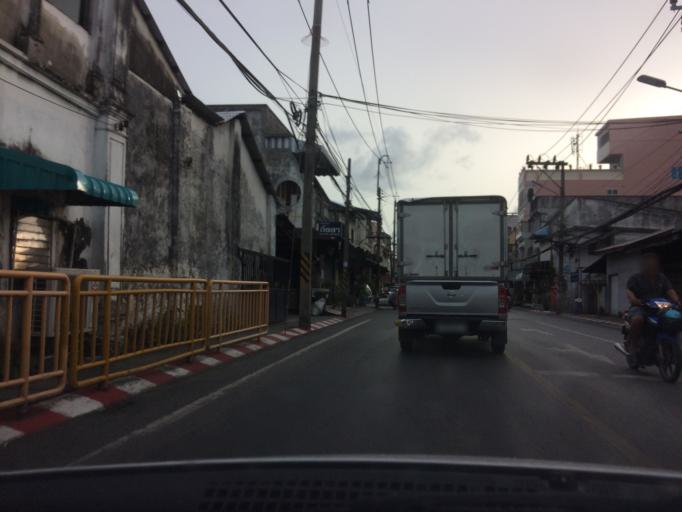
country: TH
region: Phuket
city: Ban Talat Yai
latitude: 7.8768
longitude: 98.3933
